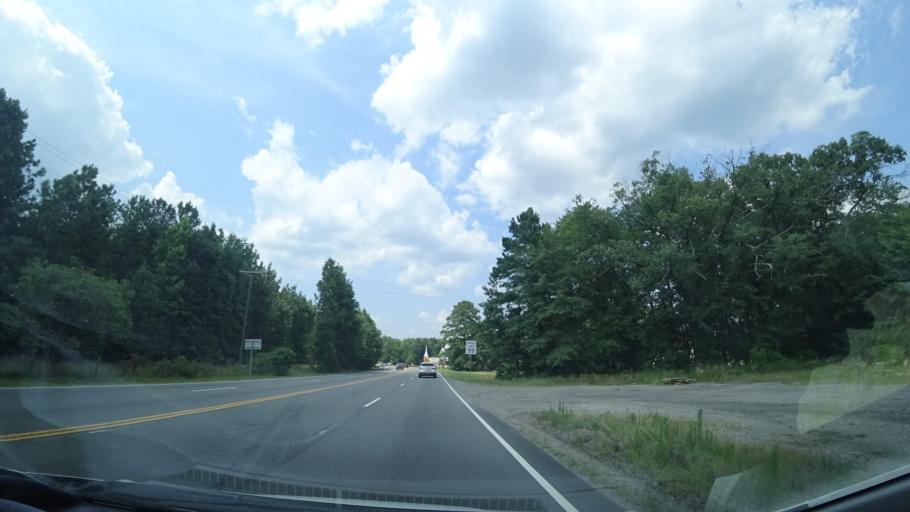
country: US
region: Virginia
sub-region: Hanover County
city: Ashland
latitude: 37.8460
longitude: -77.4638
